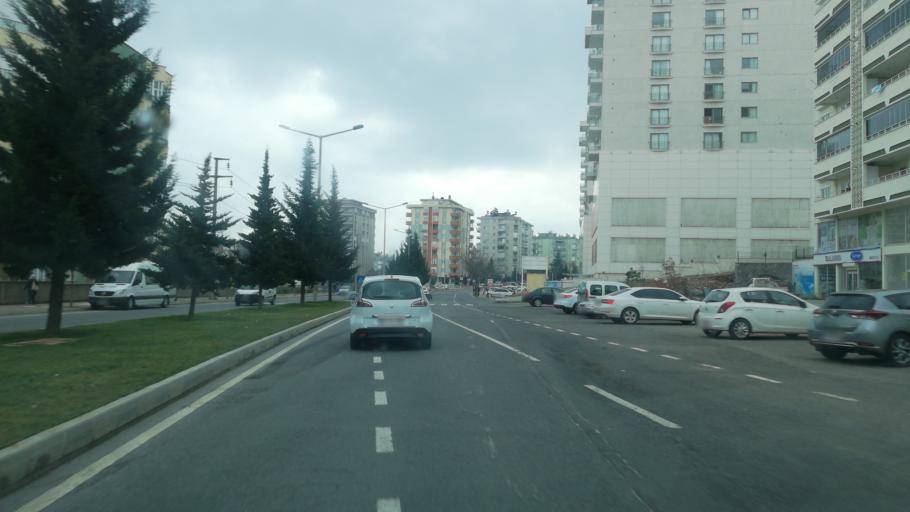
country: TR
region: Kahramanmaras
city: Kahramanmaras
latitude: 37.5903
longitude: 36.8894
